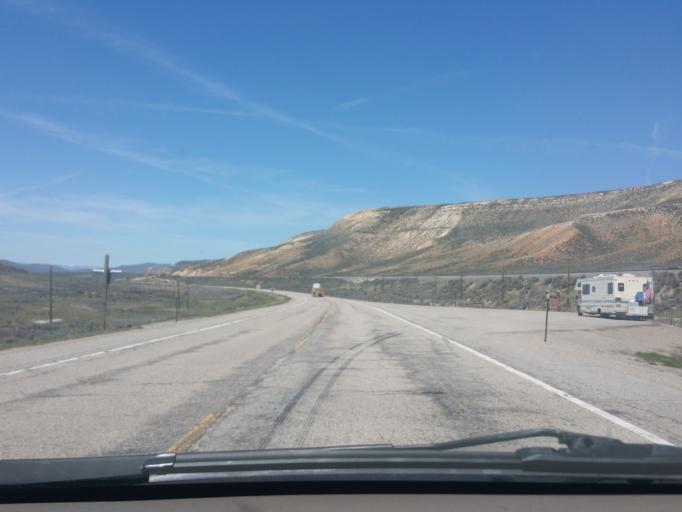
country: US
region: Wyoming
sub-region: Lincoln County
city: Kemmerer
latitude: 41.8147
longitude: -110.6290
